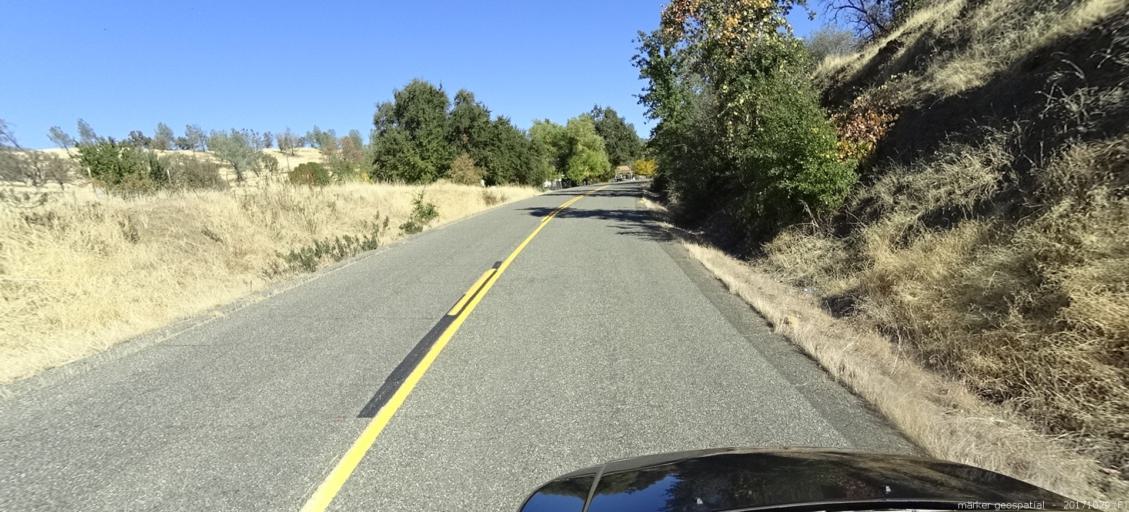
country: US
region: California
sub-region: Shasta County
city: Shasta
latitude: 40.4728
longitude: -122.6212
